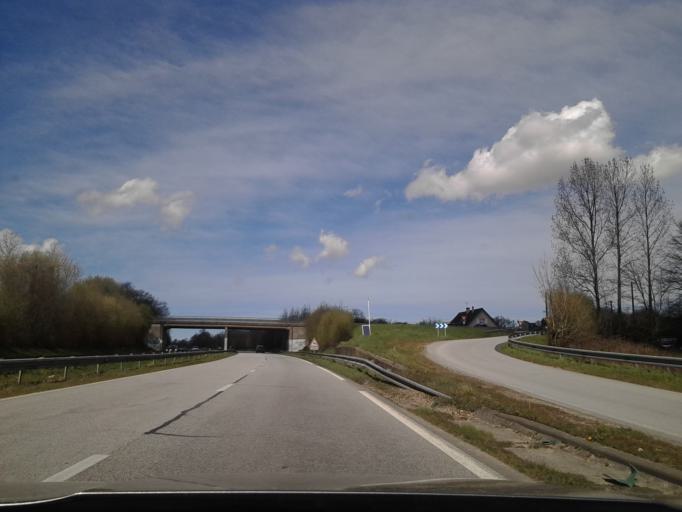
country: FR
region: Lower Normandy
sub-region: Departement de la Manche
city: Brix
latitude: 49.5629
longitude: -1.5681
